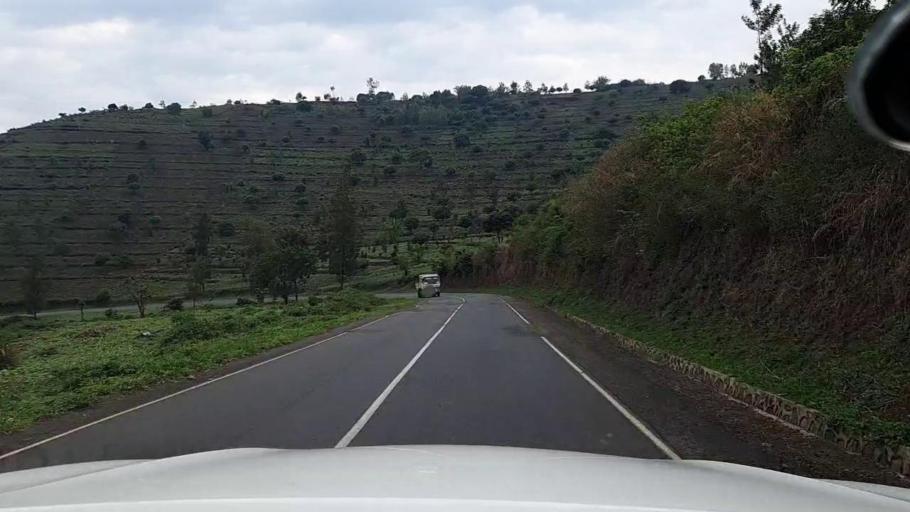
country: RW
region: Western Province
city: Cyangugu
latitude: -2.6735
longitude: 29.0032
